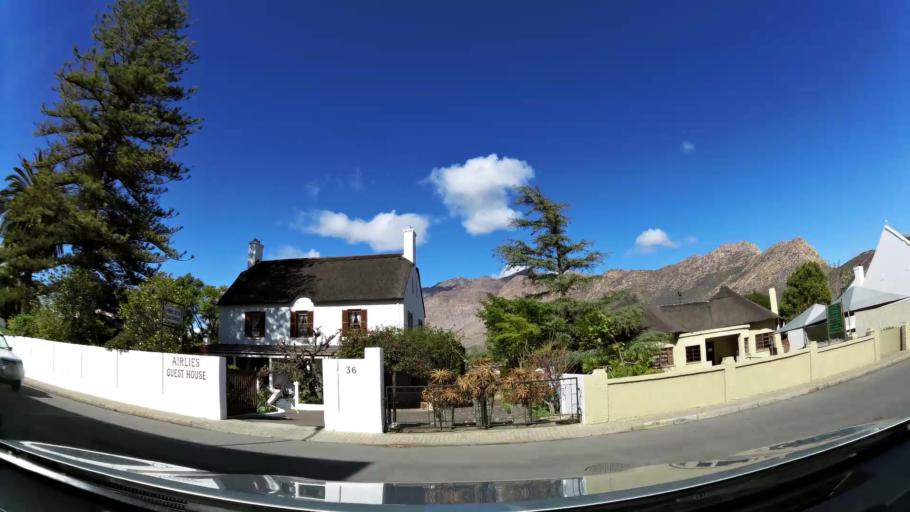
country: ZA
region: Western Cape
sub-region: Cape Winelands District Municipality
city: Ashton
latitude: -33.7871
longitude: 20.1197
